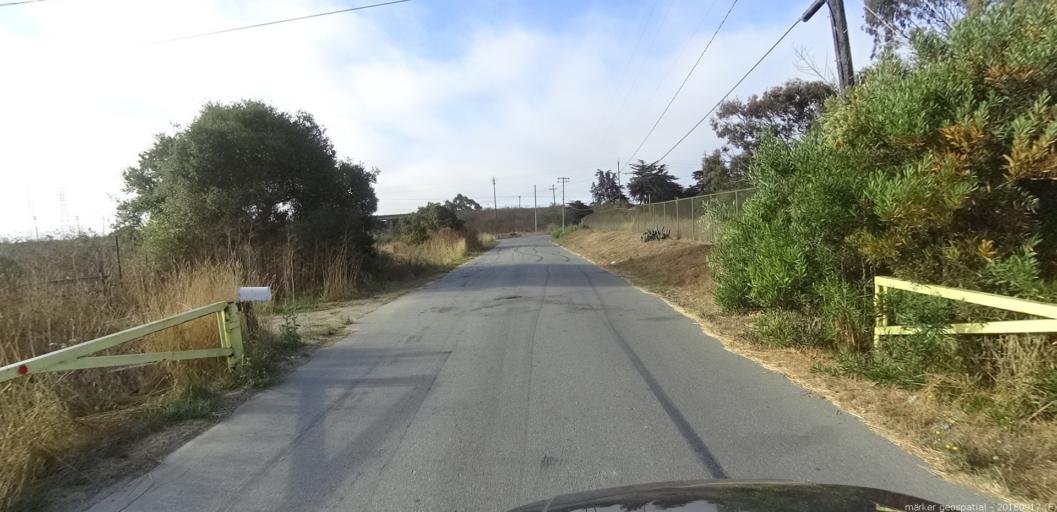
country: US
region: California
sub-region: Monterey County
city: Elkhorn
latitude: 36.7985
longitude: -121.7539
